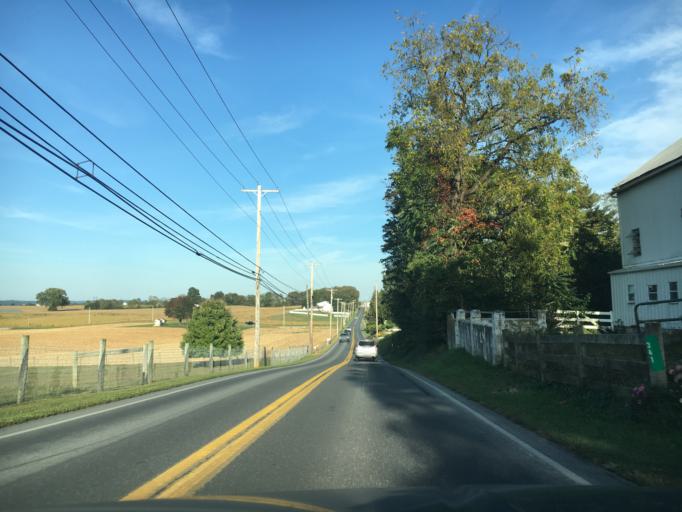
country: US
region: Pennsylvania
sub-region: Lancaster County
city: Ephrata
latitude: 40.1335
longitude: -76.1394
